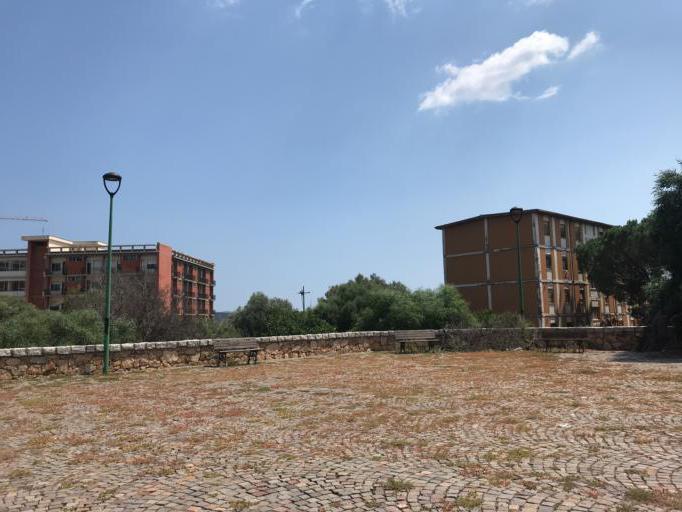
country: IT
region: Sardinia
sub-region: Provincia di Olbia-Tempio
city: Olbia
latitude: 40.9105
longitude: 9.5129
